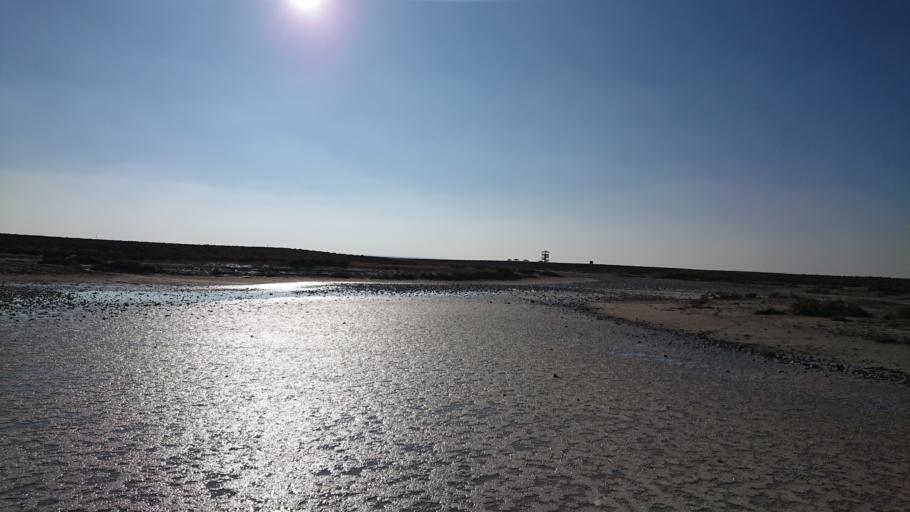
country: TR
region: Aksaray
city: Eskil
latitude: 38.4278
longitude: 33.5058
